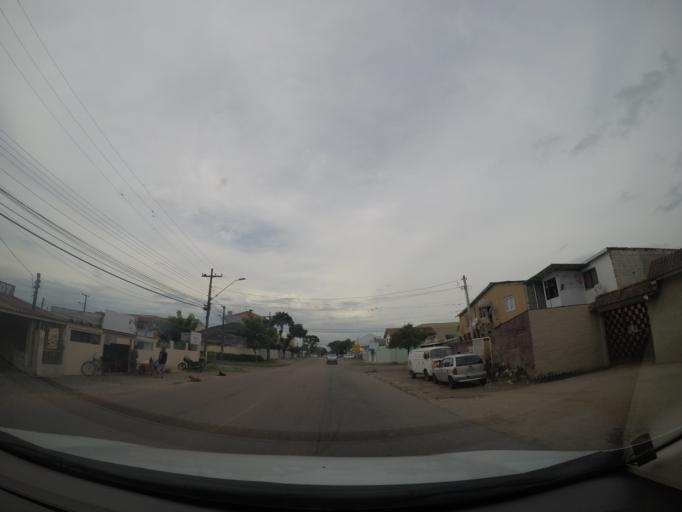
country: BR
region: Parana
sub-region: Sao Jose Dos Pinhais
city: Sao Jose dos Pinhais
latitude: -25.5146
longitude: -49.2218
